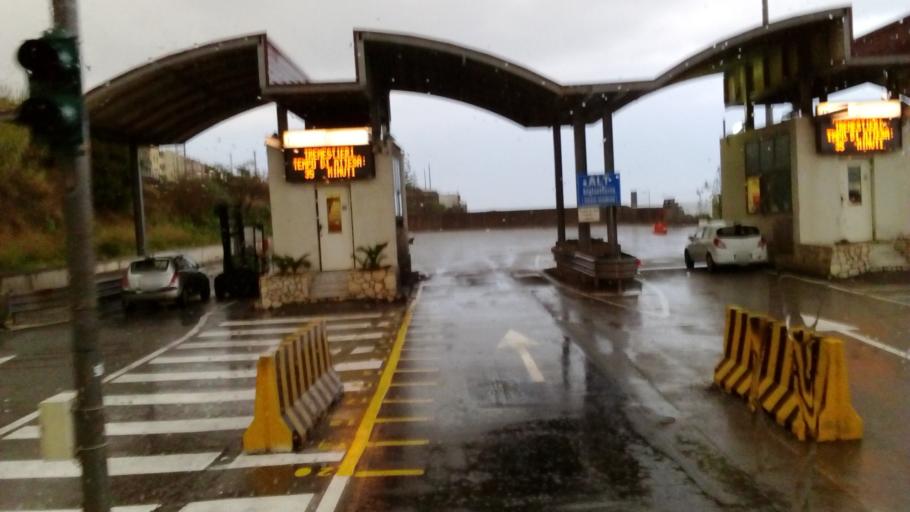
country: IT
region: Sicily
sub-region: Messina
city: Larderia
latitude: 38.1329
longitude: 15.5239
